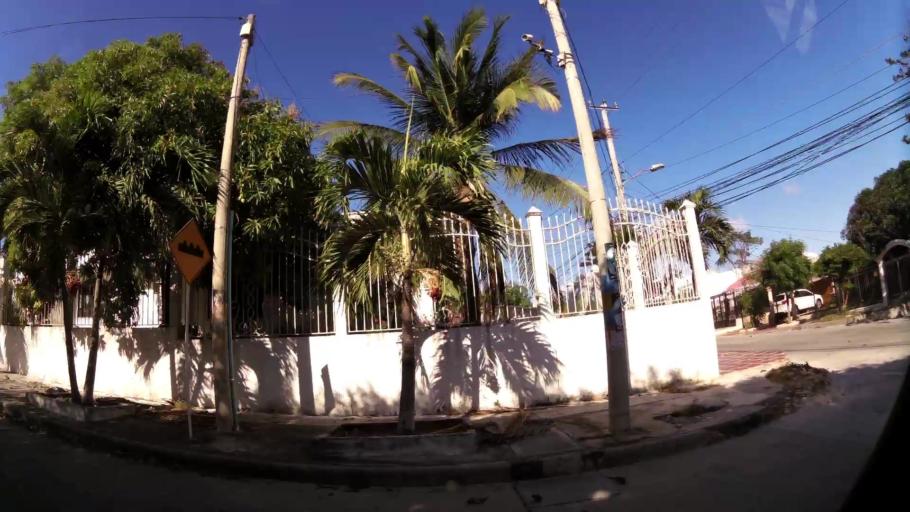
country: CO
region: Atlantico
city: Barranquilla
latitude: 10.9916
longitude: -74.8265
